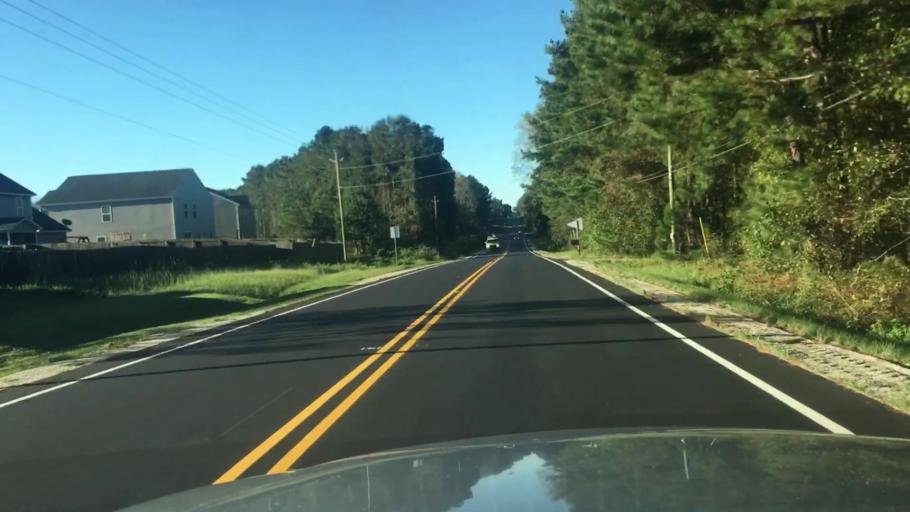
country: US
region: North Carolina
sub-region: Harnett County
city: Lillington
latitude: 35.3446
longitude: -78.8530
